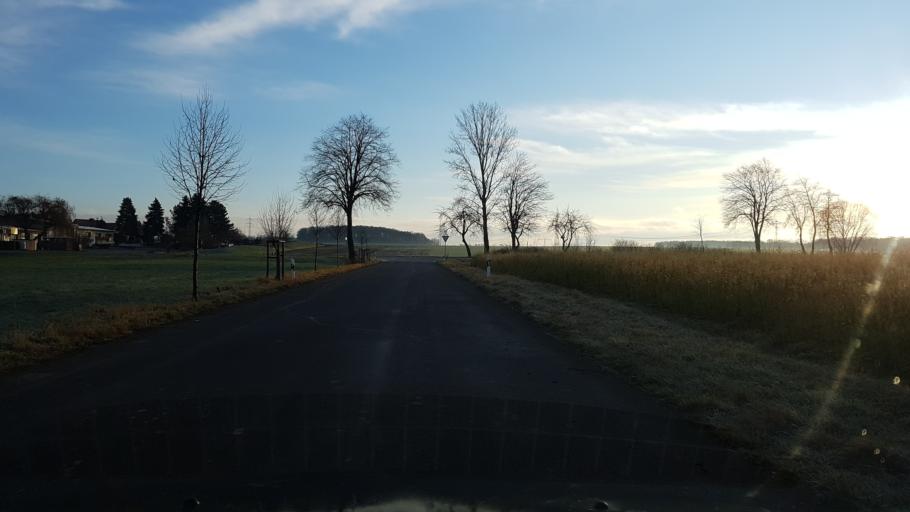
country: DE
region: Saxony
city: Neschwitz
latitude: 51.2431
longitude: 14.3443
